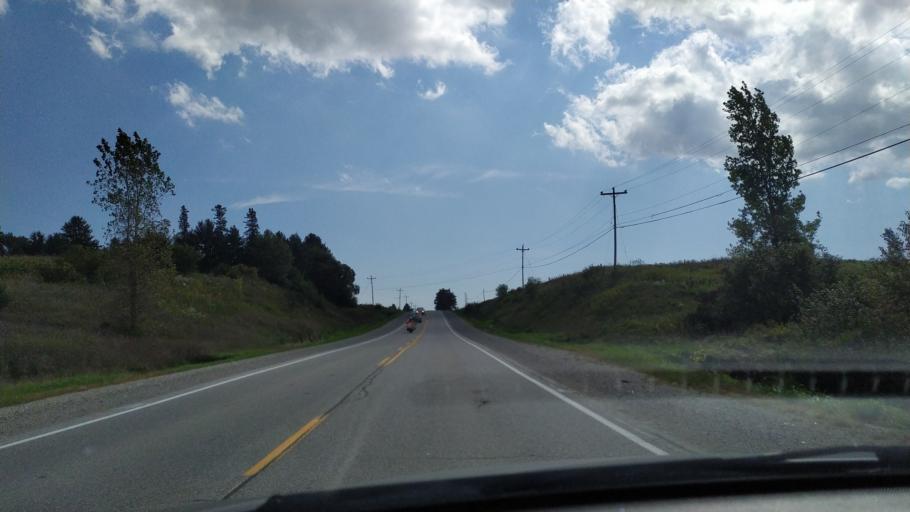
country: CA
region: Ontario
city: Ingersoll
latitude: 43.1382
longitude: -80.8925
